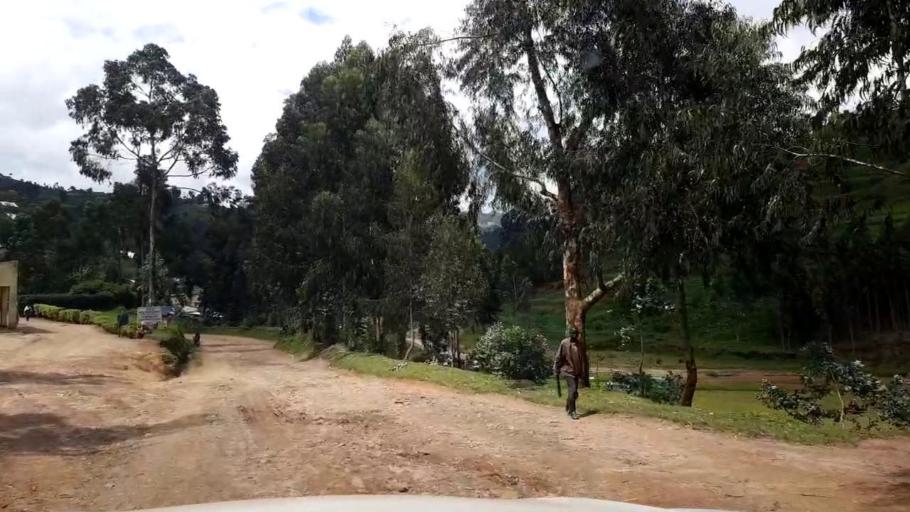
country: RW
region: Western Province
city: Kibuye
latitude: -1.9161
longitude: 29.4578
